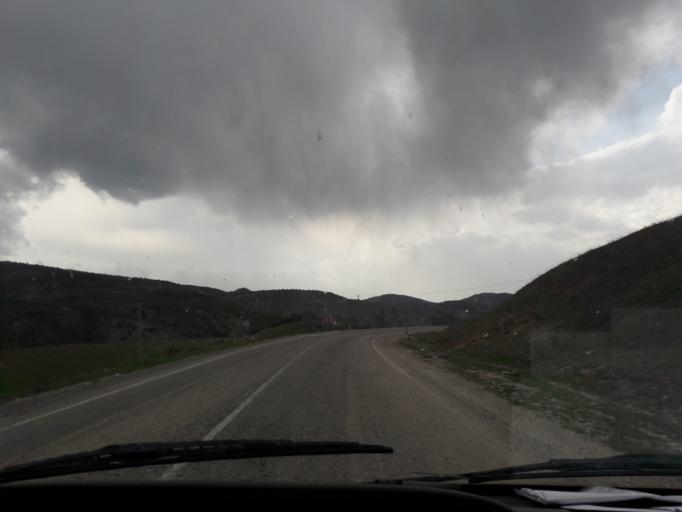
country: TR
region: Giresun
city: Alucra
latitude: 40.2983
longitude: 38.7996
